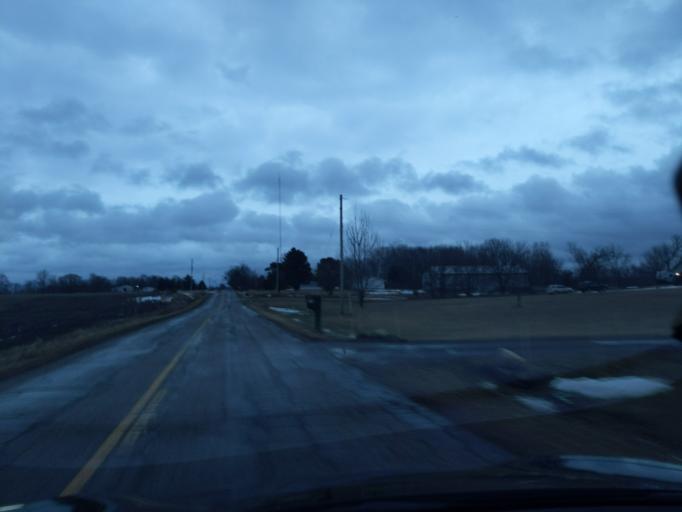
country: US
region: Michigan
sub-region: Eaton County
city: Eaton Rapids
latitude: 42.4438
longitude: -84.5892
